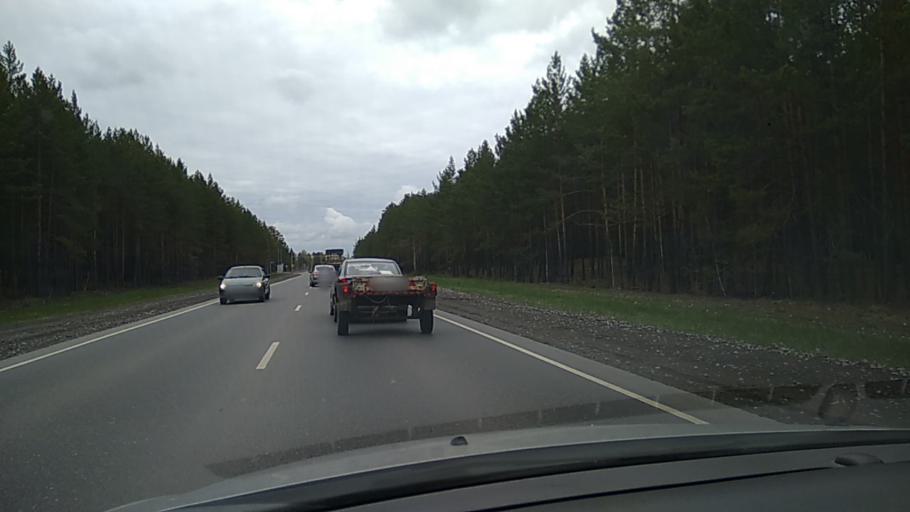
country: RU
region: Tjumen
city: Chervishevo
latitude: 57.0012
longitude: 65.4847
